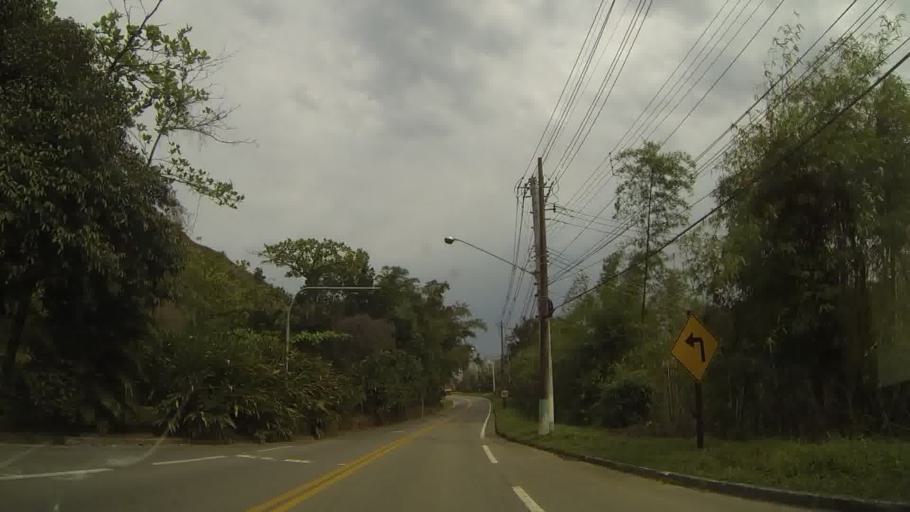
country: BR
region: Sao Paulo
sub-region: Sao Sebastiao
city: Sao Sebastiao
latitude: -23.8105
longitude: -45.5397
